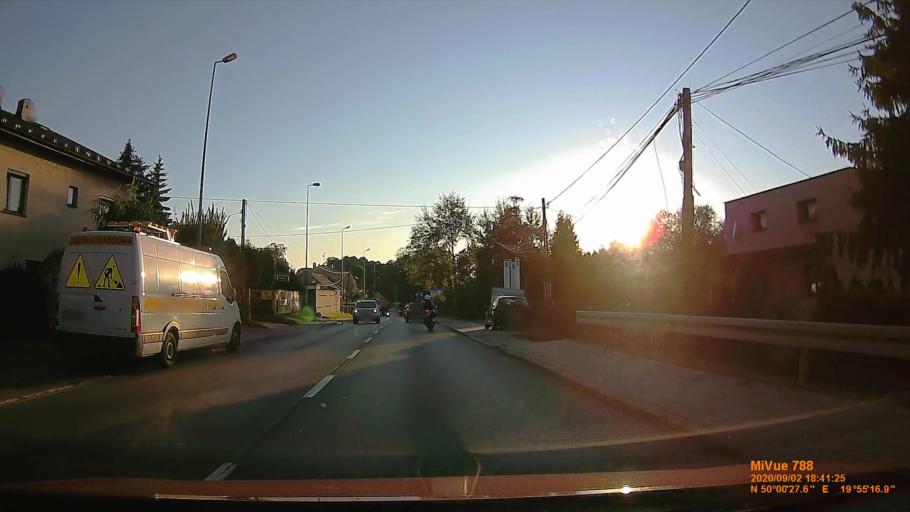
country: PL
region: Lesser Poland Voivodeship
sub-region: Powiat krakowski
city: Libertow
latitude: 50.0076
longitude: 19.9211
